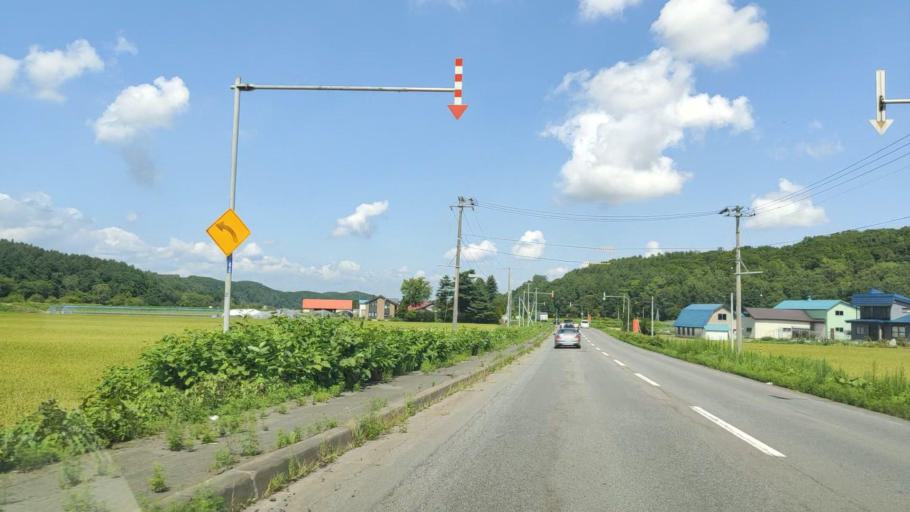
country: JP
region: Hokkaido
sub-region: Asahikawa-shi
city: Asahikawa
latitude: 43.6266
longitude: 142.4656
